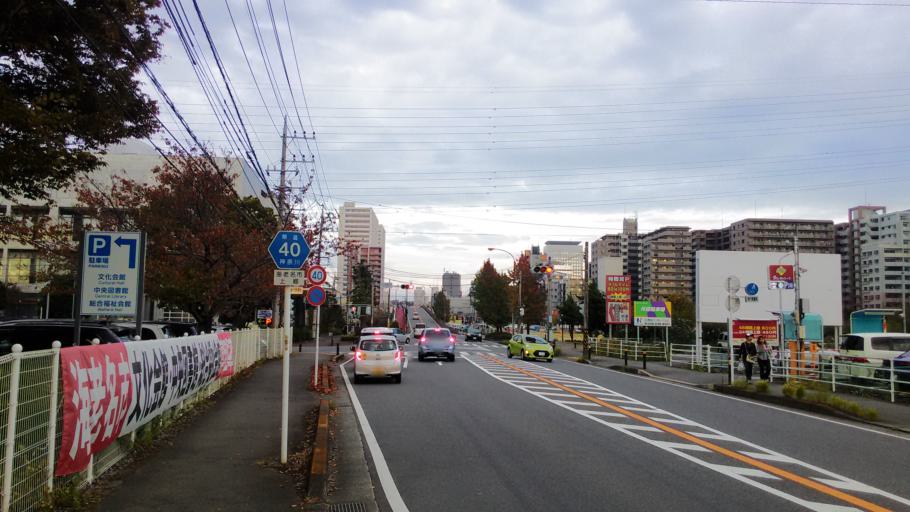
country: JP
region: Kanagawa
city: Atsugi
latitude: 35.4510
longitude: 139.3852
